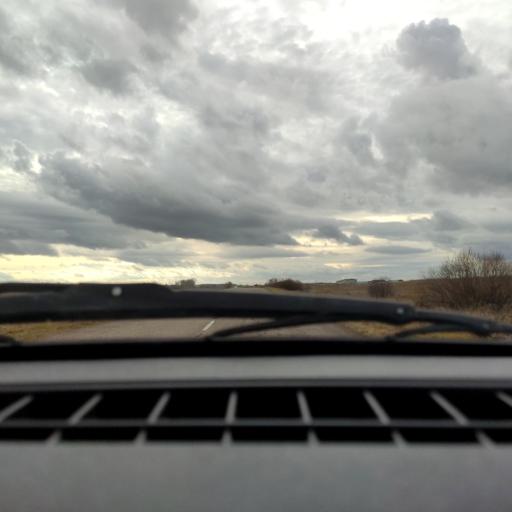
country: RU
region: Bashkortostan
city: Asanovo
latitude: 54.9191
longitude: 55.5085
